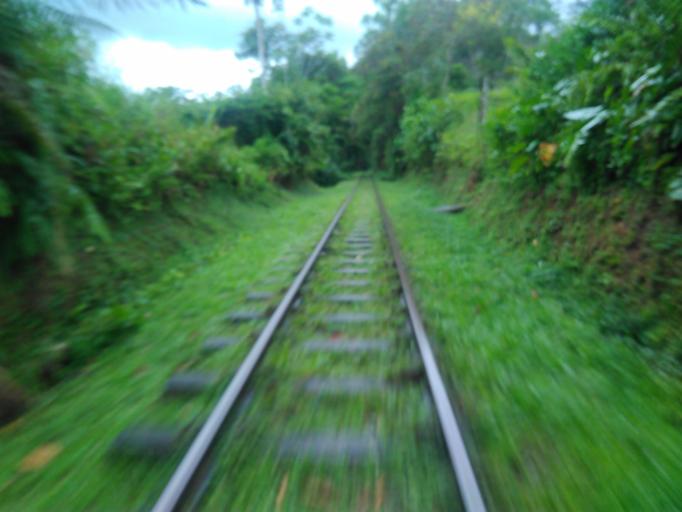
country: CO
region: Valle del Cauca
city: Buenaventura
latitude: 3.8426
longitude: -76.8965
